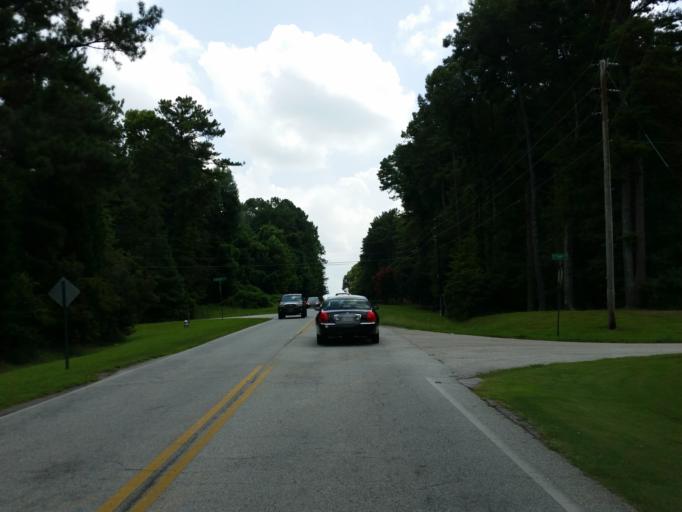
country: US
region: Georgia
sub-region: Henry County
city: Stockbridge
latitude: 33.5134
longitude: -84.2779
